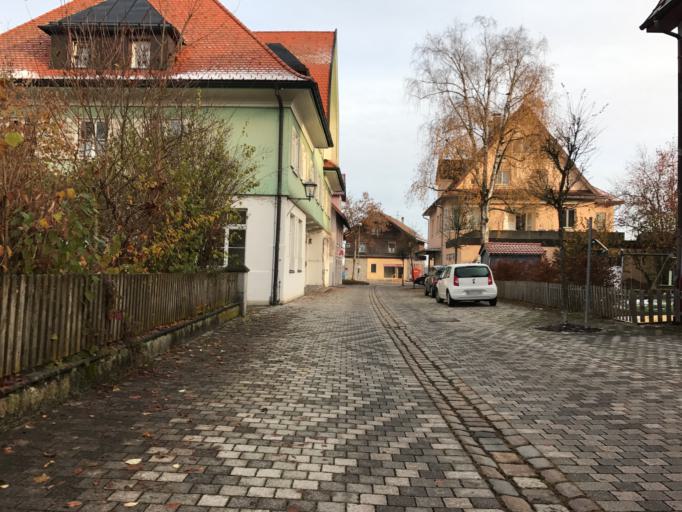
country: DE
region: Bavaria
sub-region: Swabia
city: Weiler-Simmerberg
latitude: 47.5832
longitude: 9.9173
